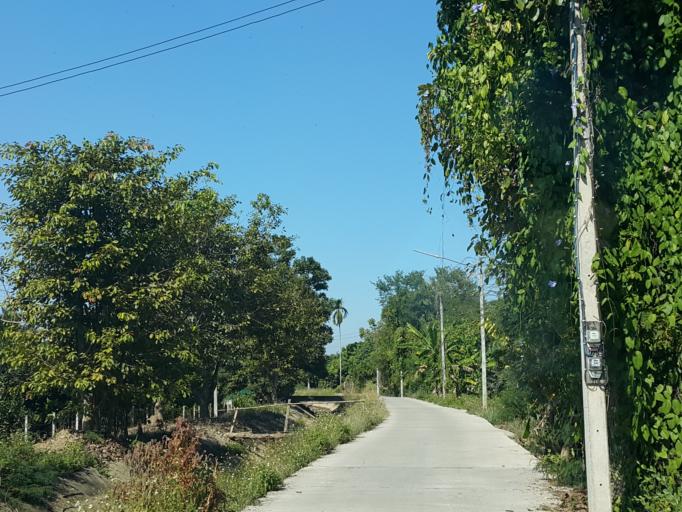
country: TH
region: Chiang Mai
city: San Sai
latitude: 18.8723
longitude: 98.9840
